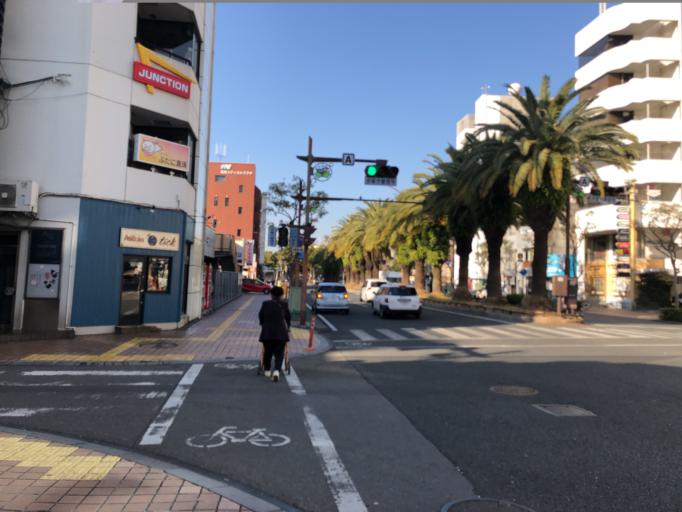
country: JP
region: Kochi
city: Kochi-shi
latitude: 33.5616
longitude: 133.5391
